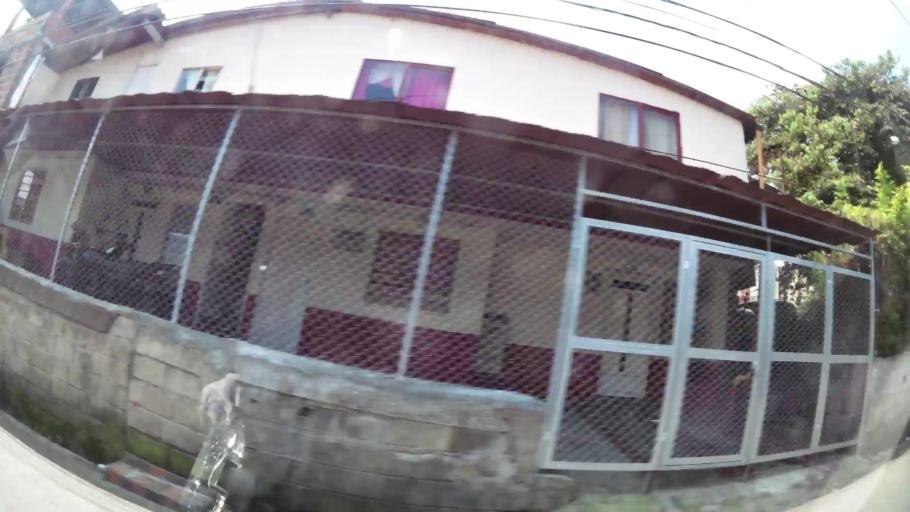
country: CO
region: Antioquia
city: La Estrella
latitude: 6.1780
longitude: -75.6461
